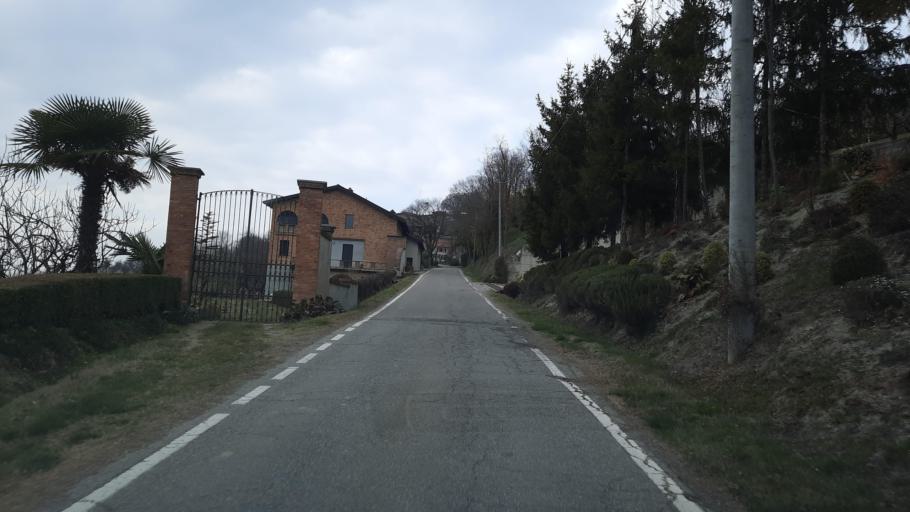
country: IT
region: Piedmont
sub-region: Provincia di Alessandria
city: Odalengo Grande
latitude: 45.1070
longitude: 8.1699
